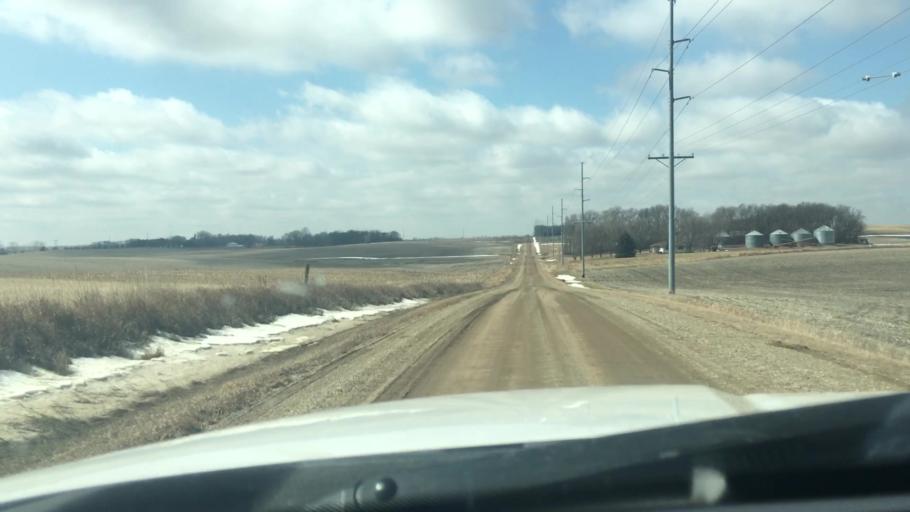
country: US
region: South Dakota
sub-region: Minnehaha County
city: Crooks
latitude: 43.6164
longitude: -96.7930
